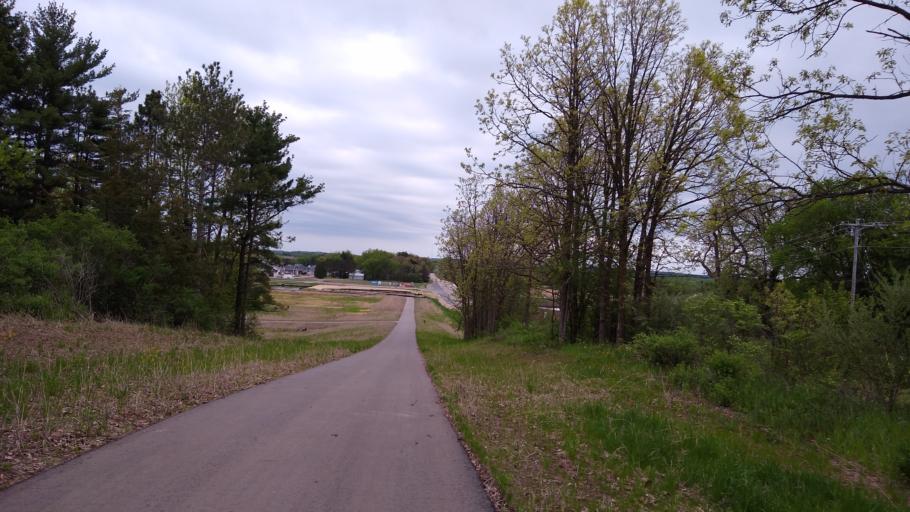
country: US
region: Wisconsin
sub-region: Dane County
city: Monona
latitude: 43.0150
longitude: -89.3754
